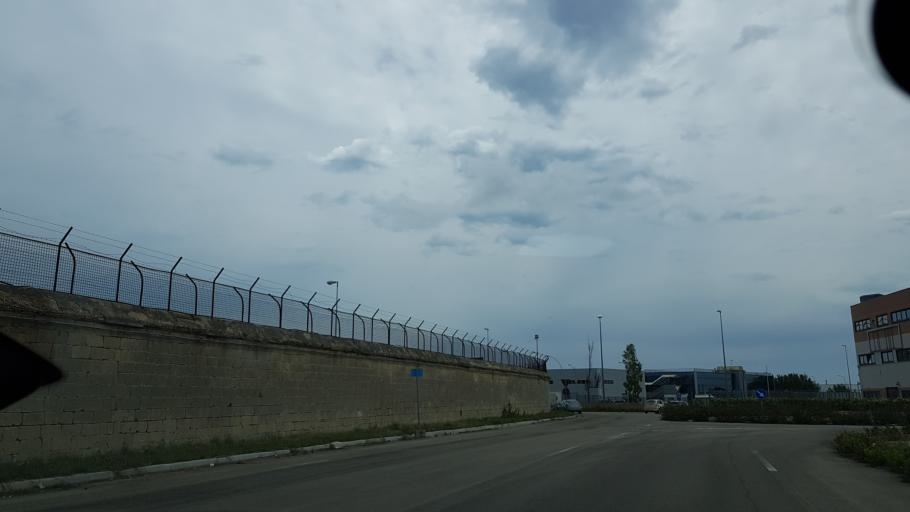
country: IT
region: Apulia
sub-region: Provincia di Brindisi
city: Materdomini
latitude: 40.6341
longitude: 17.9577
